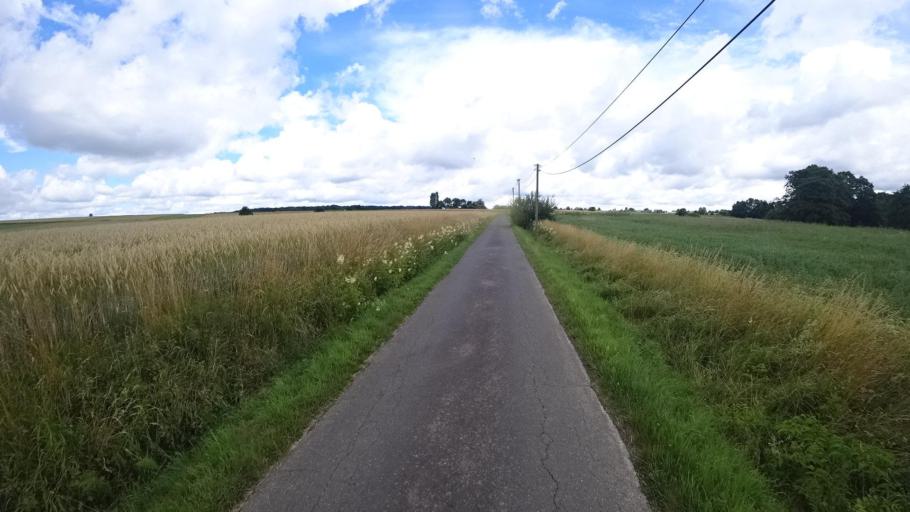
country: DE
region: Rheinland-Pfalz
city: Kircheib
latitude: 50.6984
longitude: 7.4576
